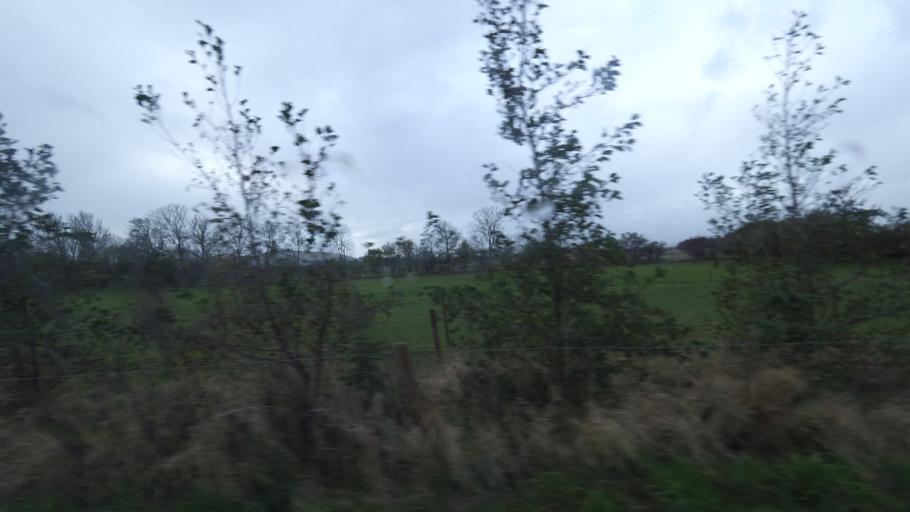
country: DK
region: Central Jutland
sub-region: Odder Kommune
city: Odder
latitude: 55.9327
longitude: 10.2359
